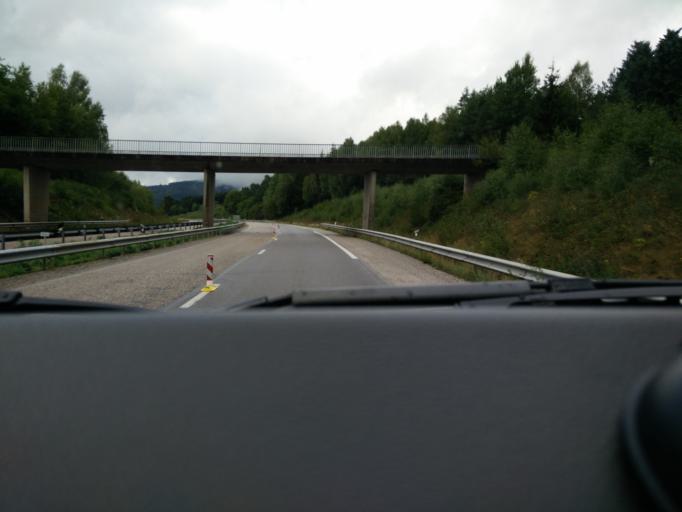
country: FR
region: Lorraine
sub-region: Departement des Vosges
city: Moyenmoutier
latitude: 48.3610
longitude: 6.8851
